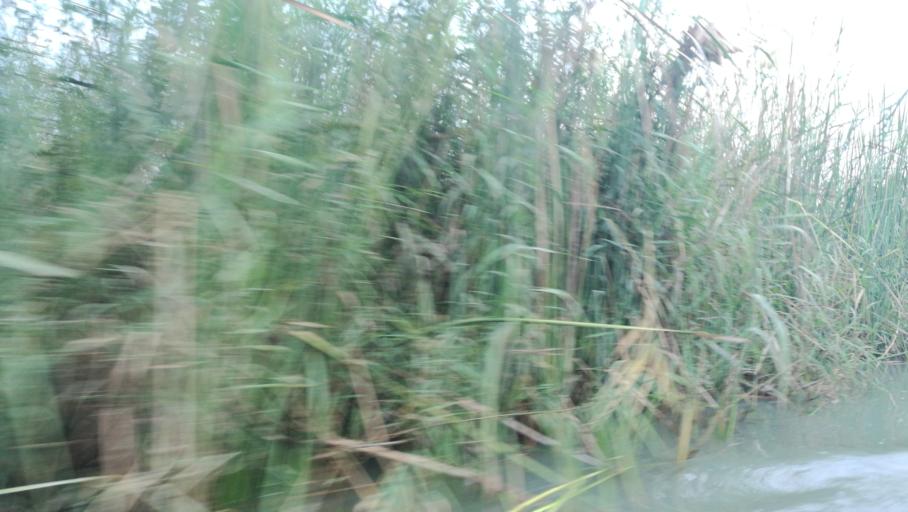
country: IQ
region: Dhi Qar
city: Al Jabayish
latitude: 30.9844
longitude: 47.0433
